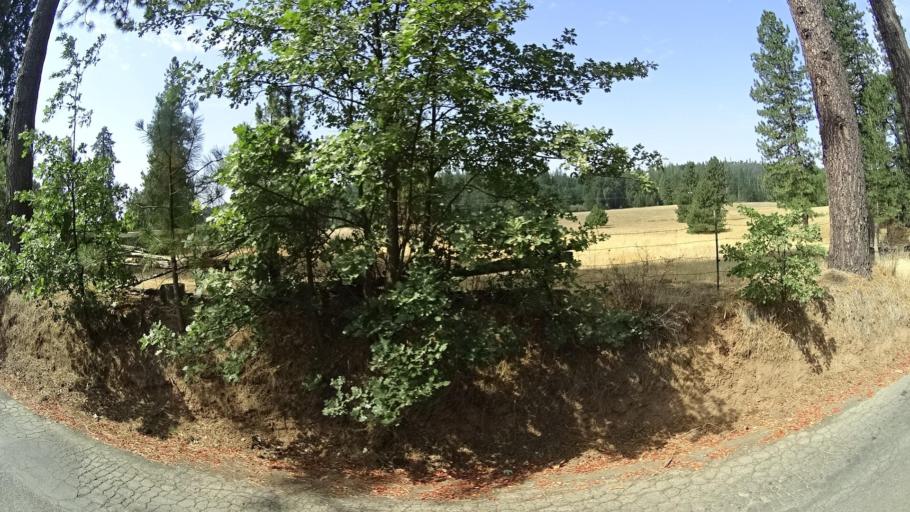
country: US
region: California
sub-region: Tuolumne County
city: Tuolumne City
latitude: 37.7620
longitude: -120.1447
